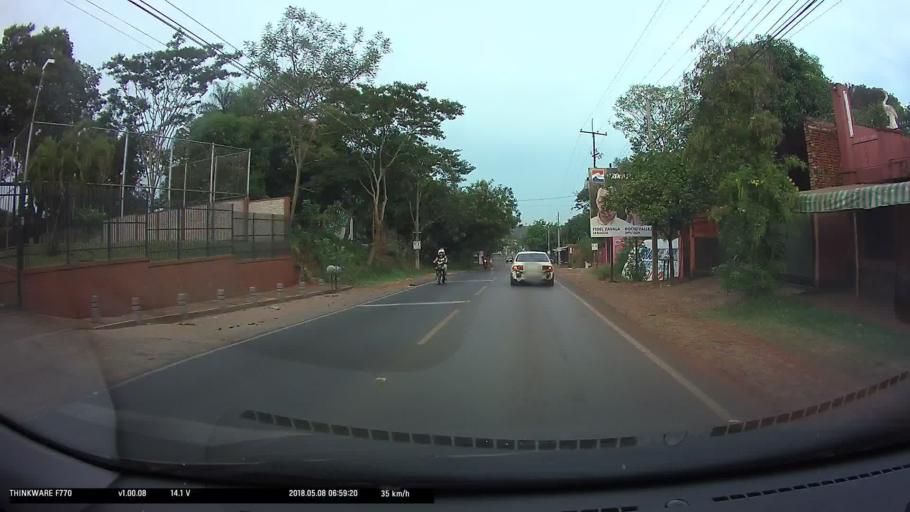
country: PY
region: Central
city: Limpio
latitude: -25.2468
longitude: -57.4839
